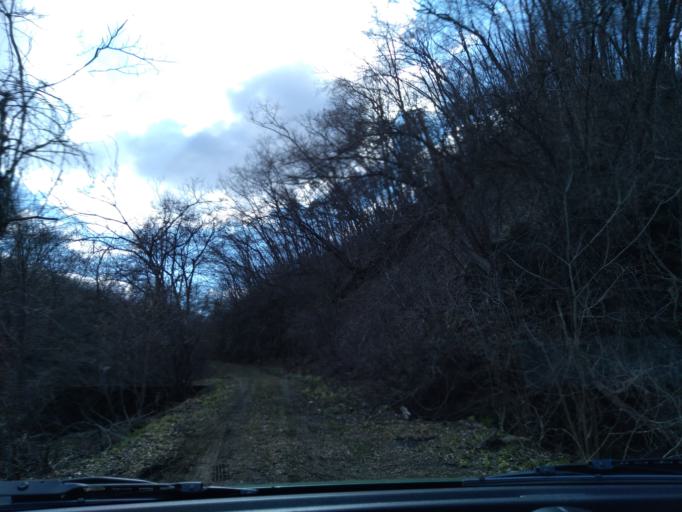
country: JP
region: Iwate
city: Ichinoseki
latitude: 38.9854
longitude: 141.0237
